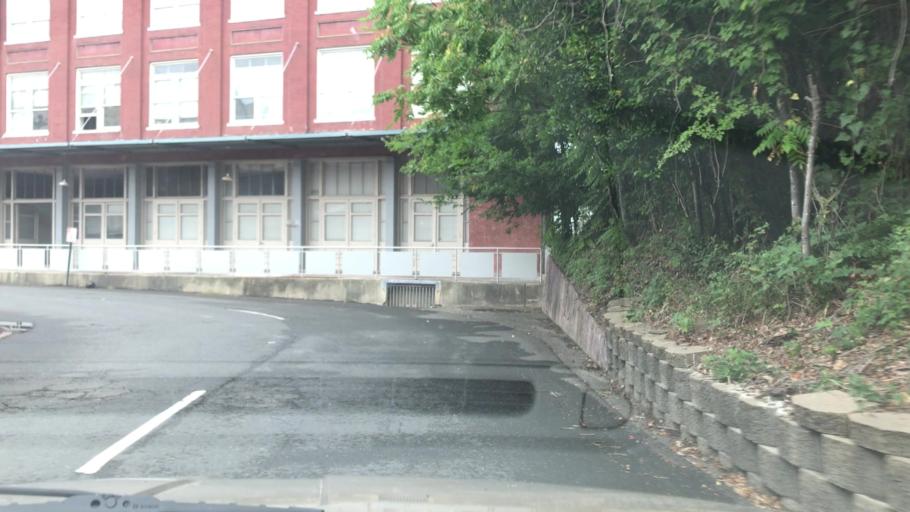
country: US
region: Louisiana
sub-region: Caddo Parish
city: Shreveport
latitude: 32.5111
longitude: -93.7465
